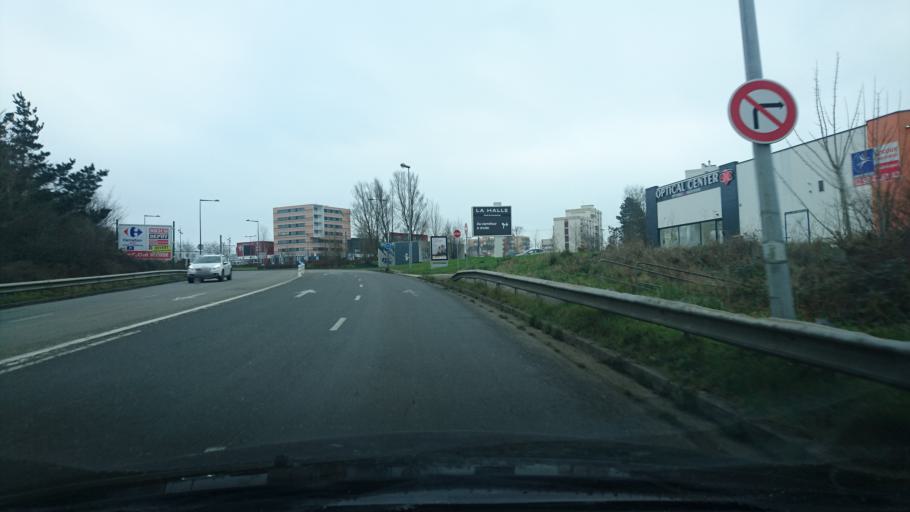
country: FR
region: Brittany
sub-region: Departement du Finistere
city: Bohars
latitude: 48.3876
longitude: -4.5305
